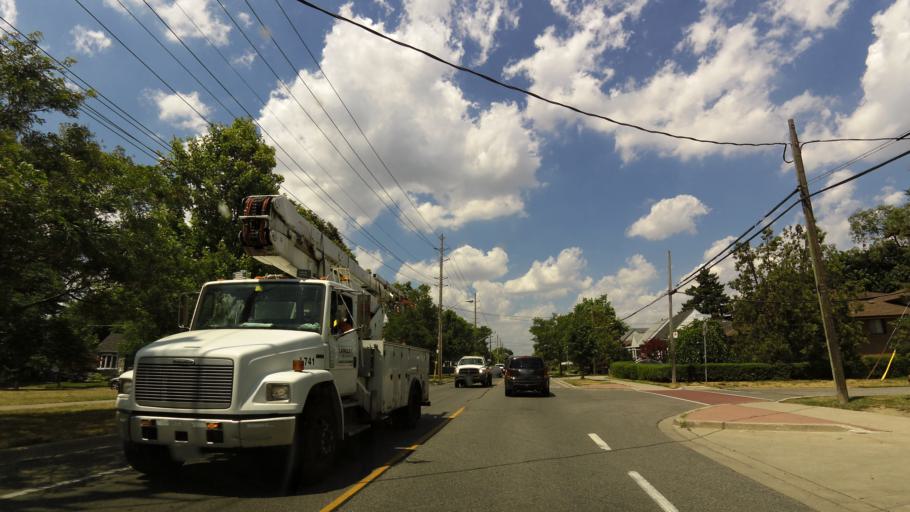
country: CA
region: Ontario
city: Etobicoke
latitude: 43.6279
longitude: -79.5033
